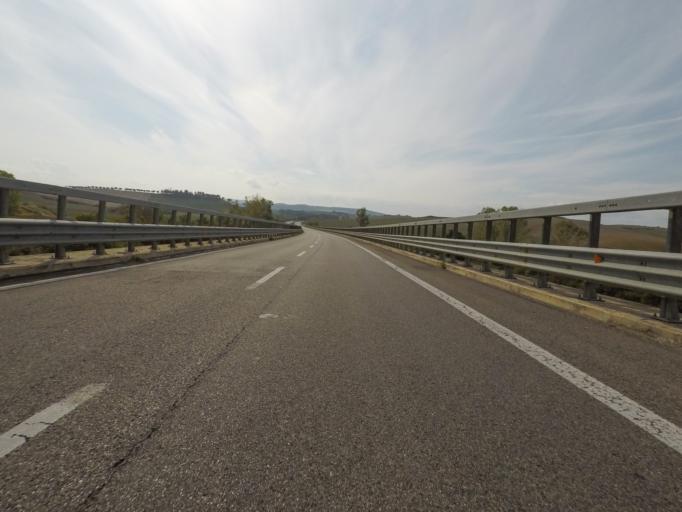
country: IT
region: Tuscany
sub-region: Provincia di Siena
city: Isola D'Arbia
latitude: 43.2668
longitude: 11.3294
